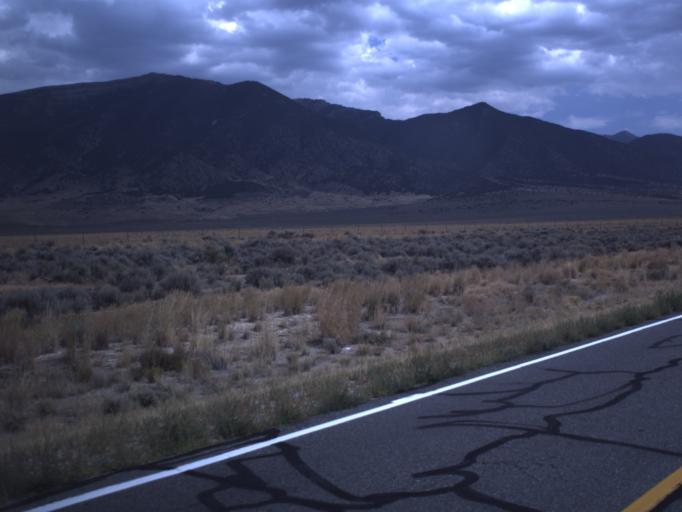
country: US
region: Utah
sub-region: Tooele County
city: Tooele
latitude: 40.3693
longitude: -112.3533
